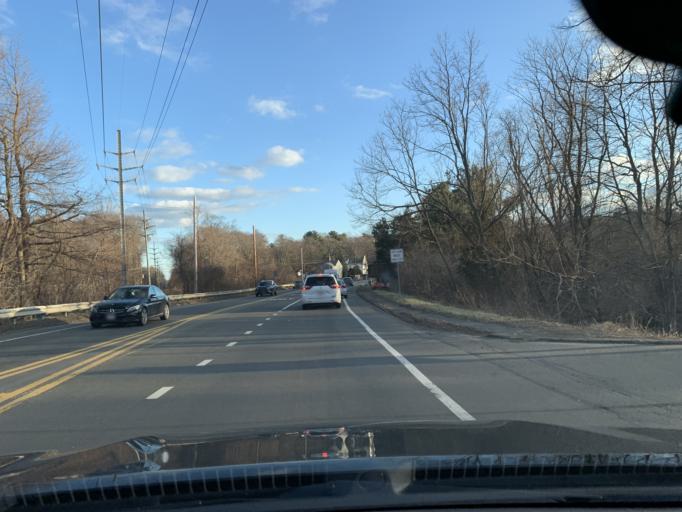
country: US
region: Massachusetts
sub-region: Essex County
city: Danvers
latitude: 42.5793
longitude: -70.9598
